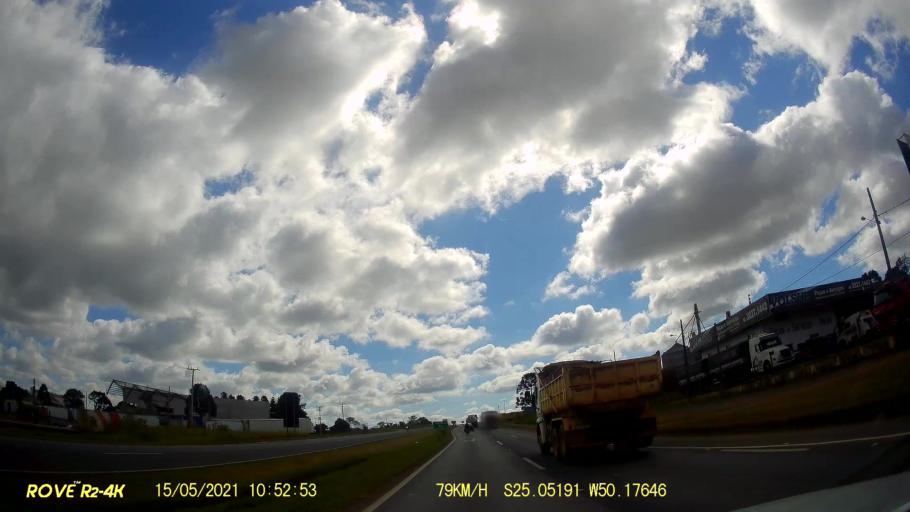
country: BR
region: Parana
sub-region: Ponta Grossa
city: Ponta Grossa
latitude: -25.0520
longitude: -50.1765
